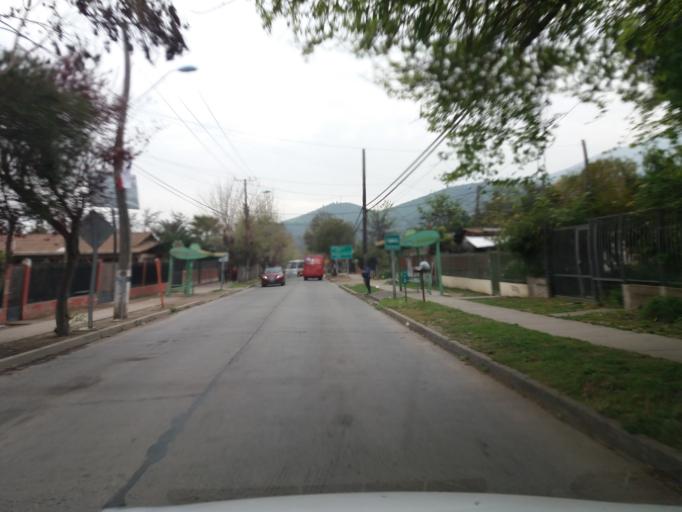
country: CL
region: Valparaiso
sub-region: Provincia de Quillota
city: Hacienda La Calera
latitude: -32.7976
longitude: -71.1467
